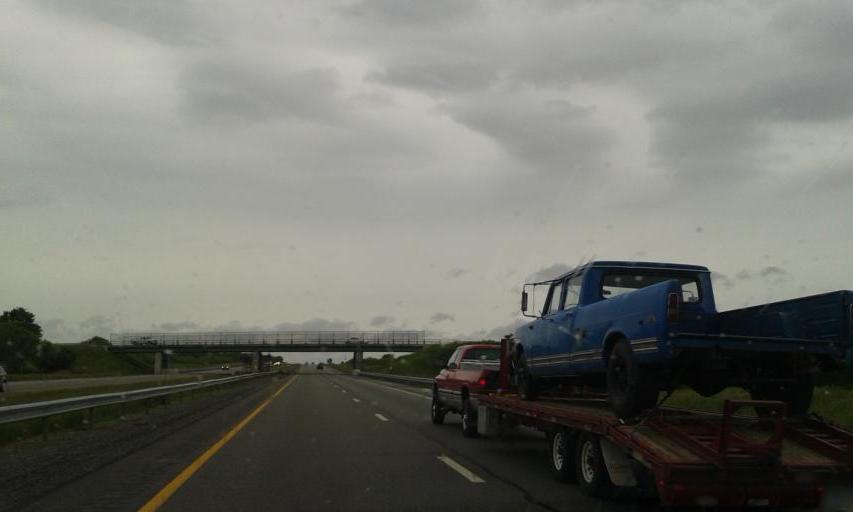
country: US
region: New York
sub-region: Genesee County
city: Batavia
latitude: 43.0210
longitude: -78.1561
